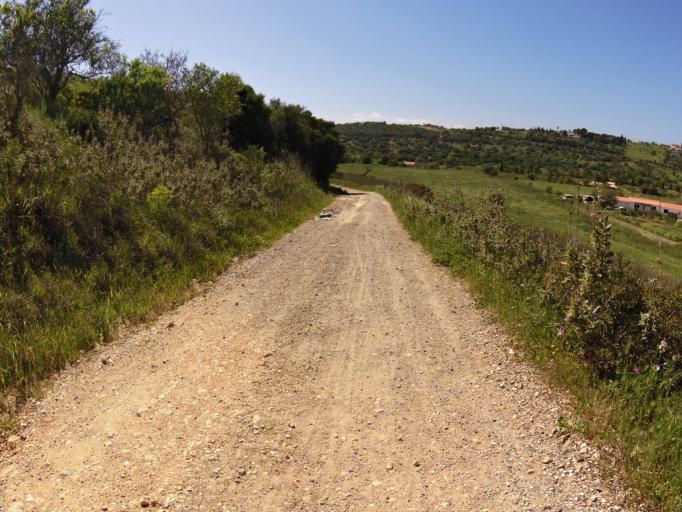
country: PT
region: Faro
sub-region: Lagos
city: Lagos
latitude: 37.1008
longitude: -8.7109
